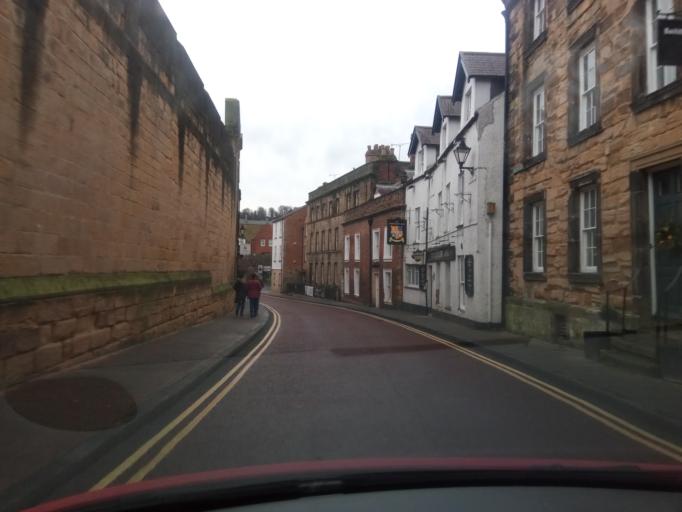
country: GB
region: England
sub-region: Northumberland
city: Alnwick
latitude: 55.4155
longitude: -1.7086
